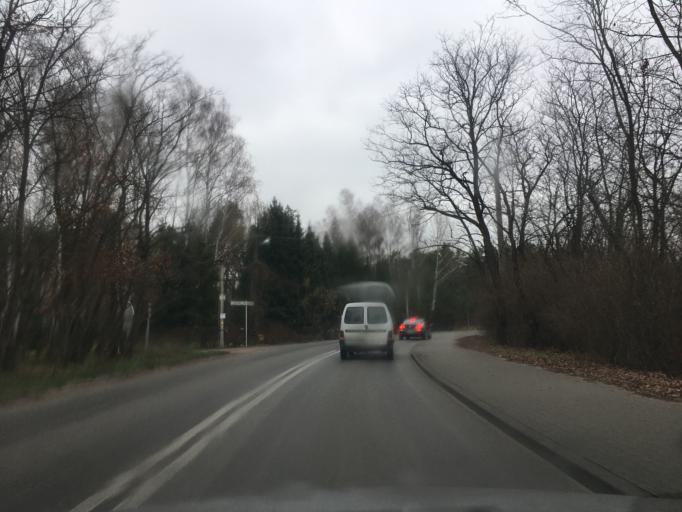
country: PL
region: Masovian Voivodeship
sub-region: Powiat piaseczynski
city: Lesznowola
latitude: 52.0623
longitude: 20.9194
